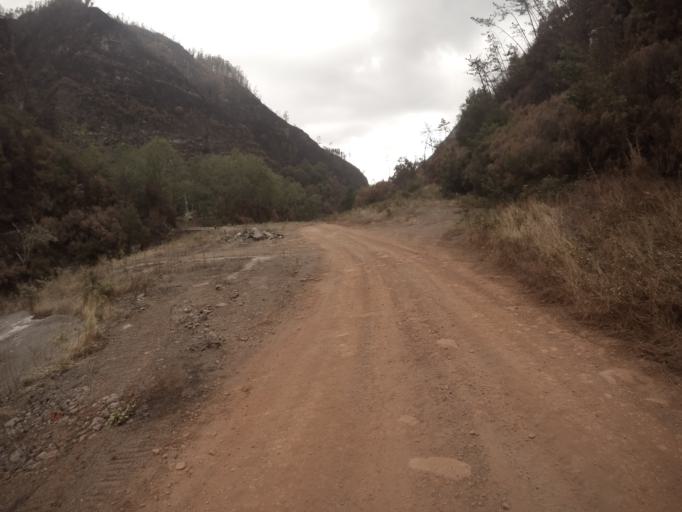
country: PT
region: Madeira
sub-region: Funchal
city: Nossa Senhora do Monte
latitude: 32.6950
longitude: -16.9173
